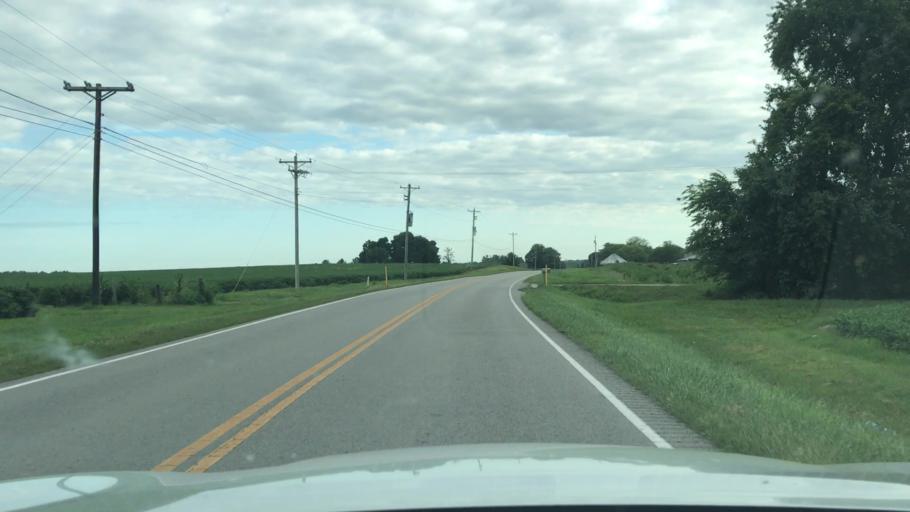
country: US
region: Kentucky
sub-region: Todd County
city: Elkton
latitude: 36.7714
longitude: -87.1666
